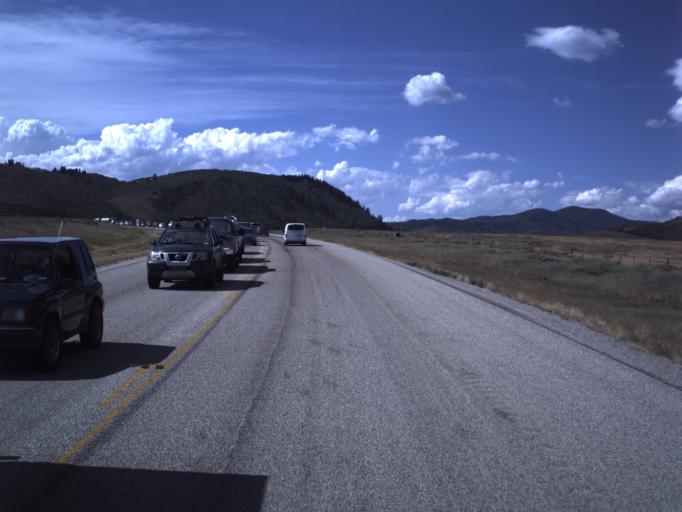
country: US
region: Utah
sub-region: Wasatch County
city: Heber
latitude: 40.2753
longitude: -111.2146
